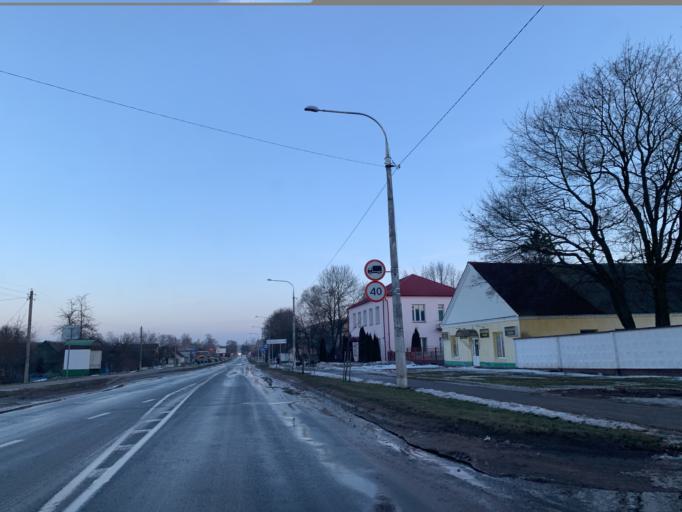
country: BY
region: Minsk
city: Nyasvizh
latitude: 53.2289
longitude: 26.6615
